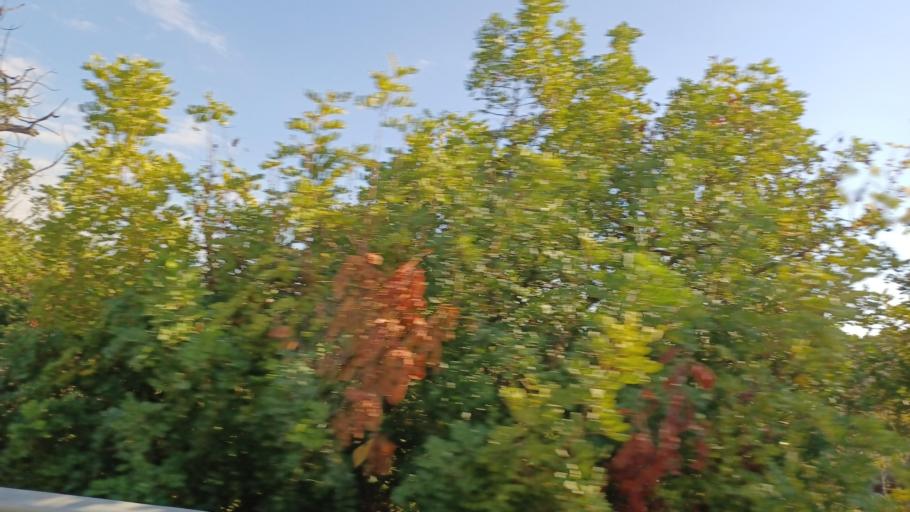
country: CY
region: Larnaka
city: Kofinou
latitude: 34.7615
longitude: 33.3223
